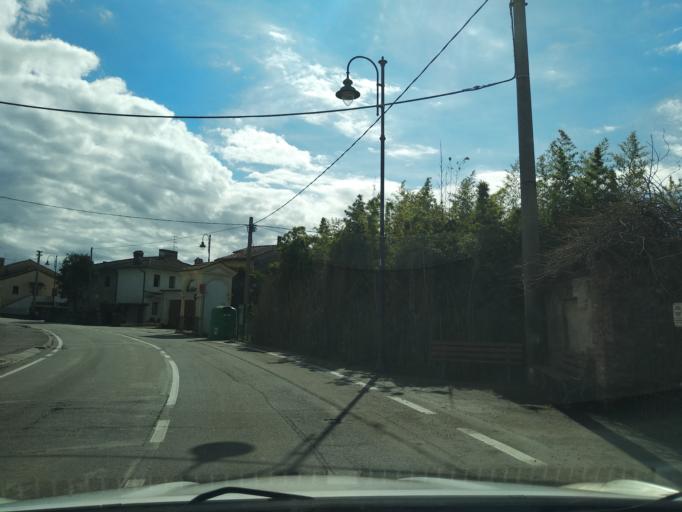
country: IT
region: Veneto
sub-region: Provincia di Vicenza
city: Bolzano Vicentino
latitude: 45.6051
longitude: 11.6110
